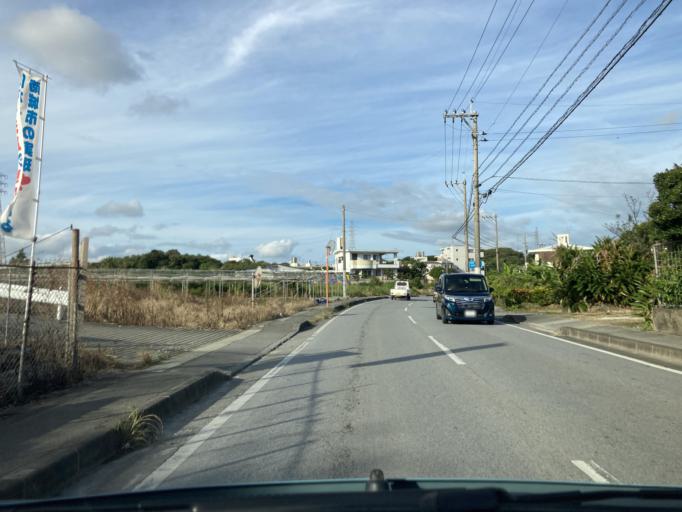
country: JP
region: Okinawa
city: Tomigusuku
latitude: 26.1615
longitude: 127.7388
